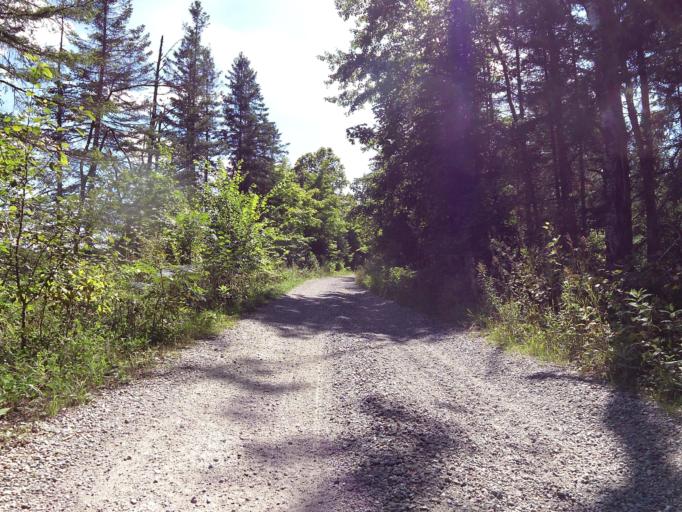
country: CA
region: Ontario
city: Renfrew
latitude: 45.0362
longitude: -76.7039
